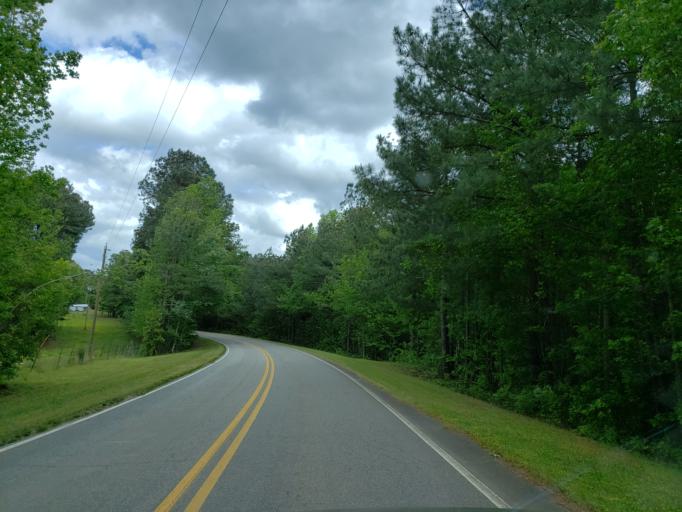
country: US
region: Georgia
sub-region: Haralson County
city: Tallapoosa
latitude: 33.6974
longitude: -85.3420
